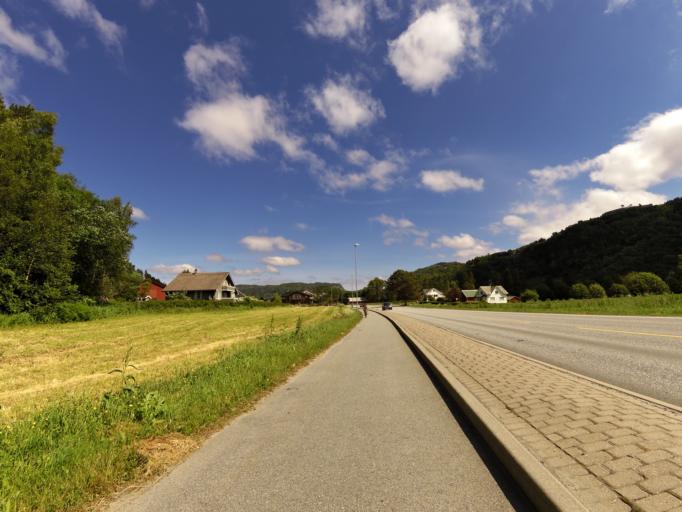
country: NO
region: Vest-Agder
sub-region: Kvinesdal
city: Liknes
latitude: 58.3057
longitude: 6.9536
